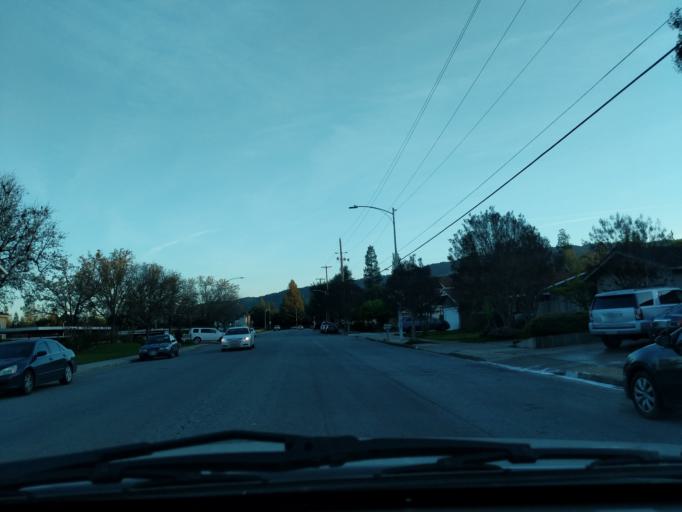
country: US
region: California
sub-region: Santa Clara County
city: Gilroy
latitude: 37.0159
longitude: -121.5916
